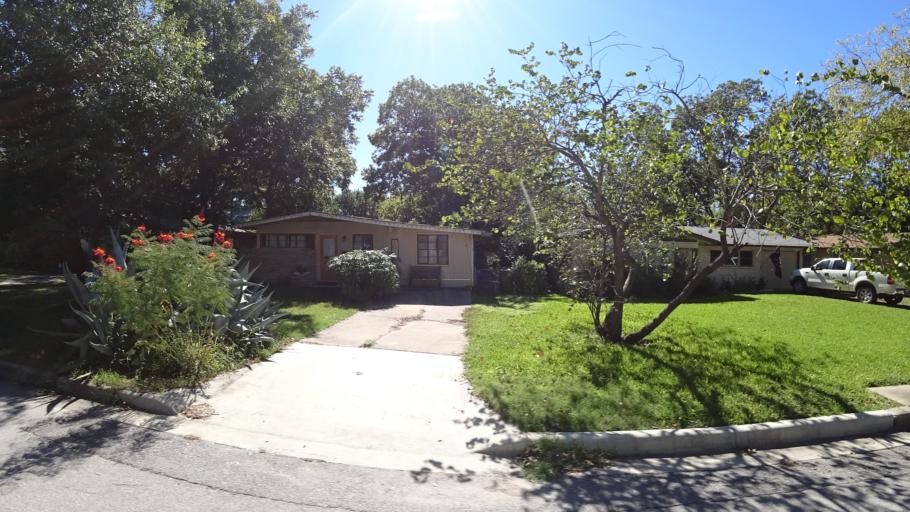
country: US
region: Texas
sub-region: Travis County
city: Austin
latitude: 30.3323
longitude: -97.7258
